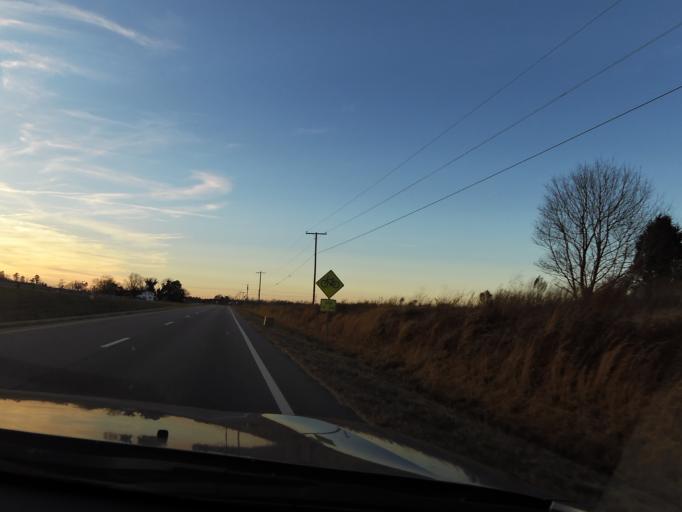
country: US
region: Virginia
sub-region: City of Franklin
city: Franklin
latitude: 36.6855
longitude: -76.9709
